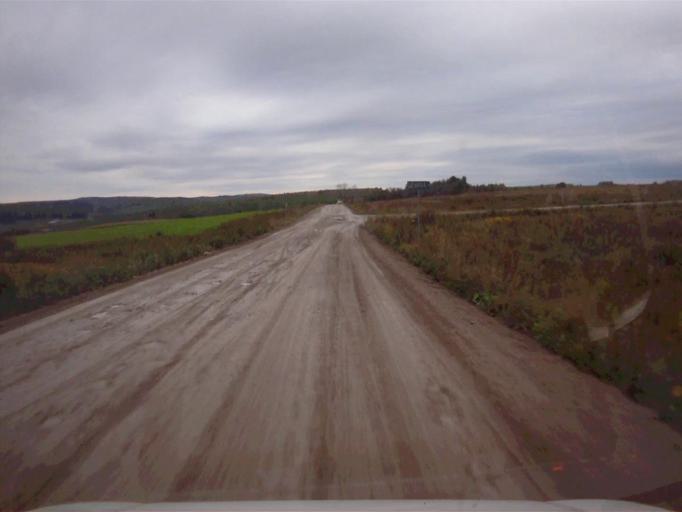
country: RU
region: Sverdlovsk
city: Mikhaylovsk
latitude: 56.1817
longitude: 59.1852
